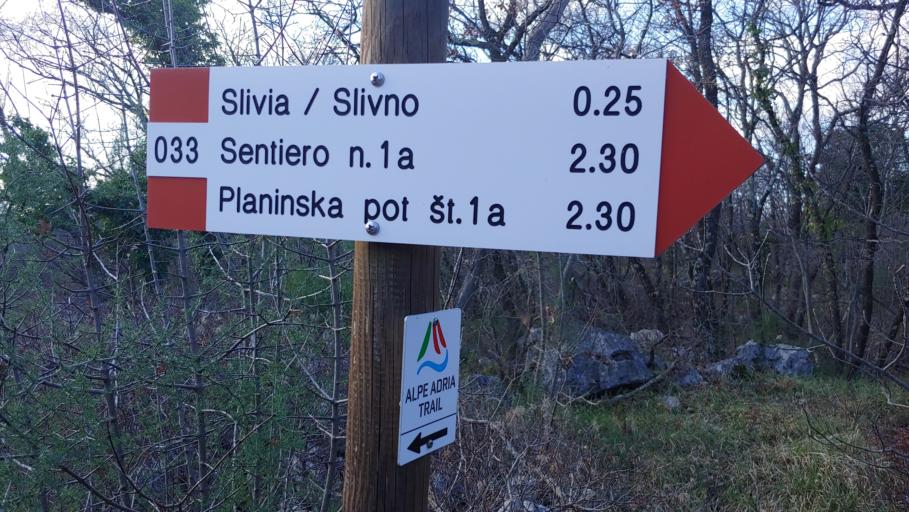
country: IT
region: Friuli Venezia Giulia
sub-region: Provincia di Trieste
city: Aurisina
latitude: 45.7652
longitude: 13.6749
